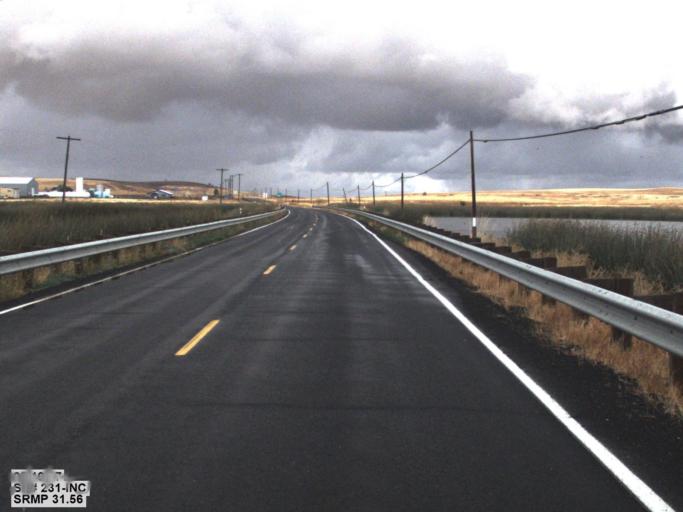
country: US
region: Washington
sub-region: Spokane County
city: Medical Lake
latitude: 47.6764
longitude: -117.8782
